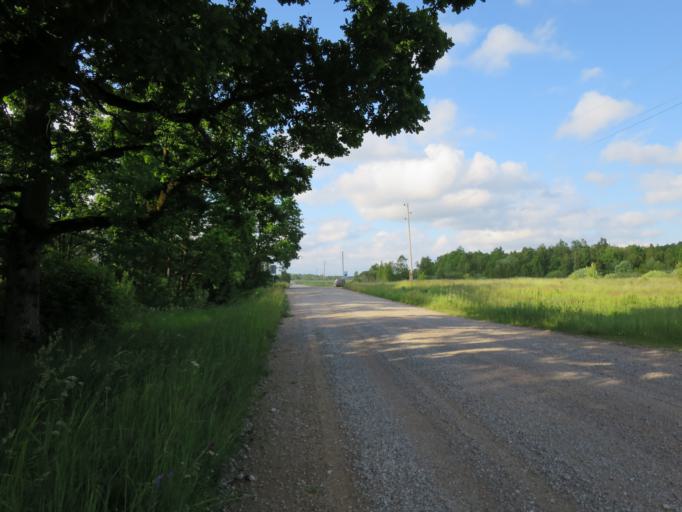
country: LV
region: Aizpute
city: Aizpute
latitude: 56.7872
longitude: 21.4925
